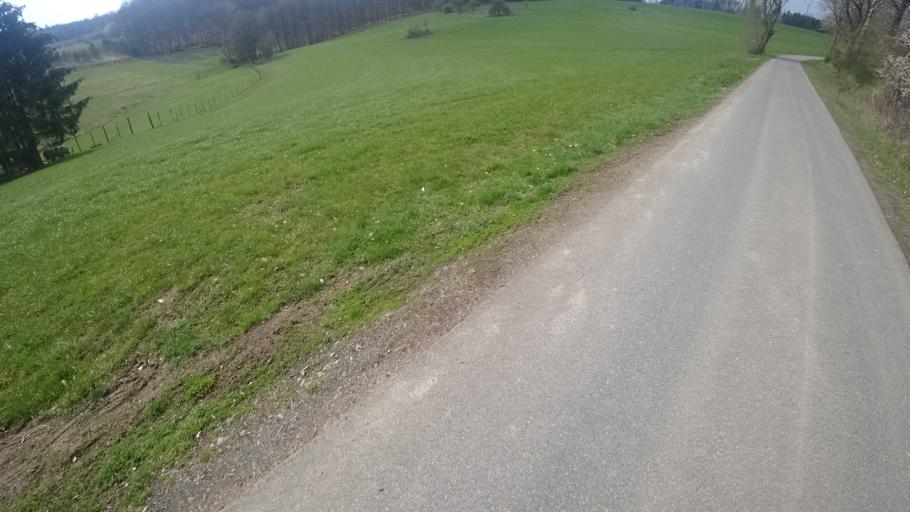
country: DE
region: Rheinland-Pfalz
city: Gebhardshain
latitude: 50.7356
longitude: 7.8228
